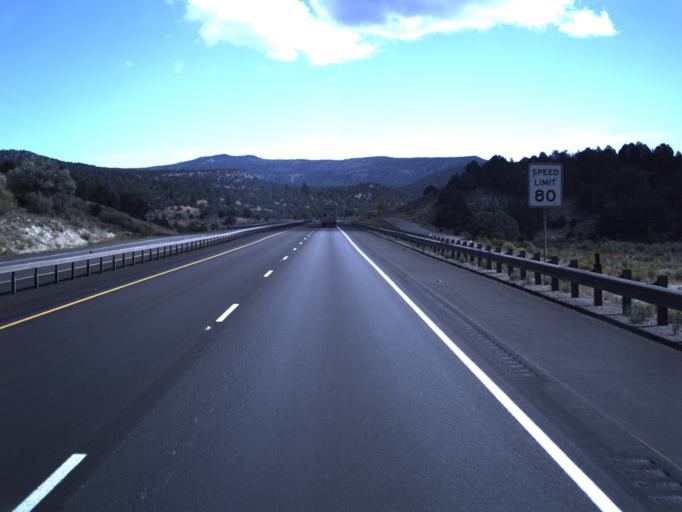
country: US
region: Utah
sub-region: Sevier County
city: Salina
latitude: 38.8818
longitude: -111.5802
